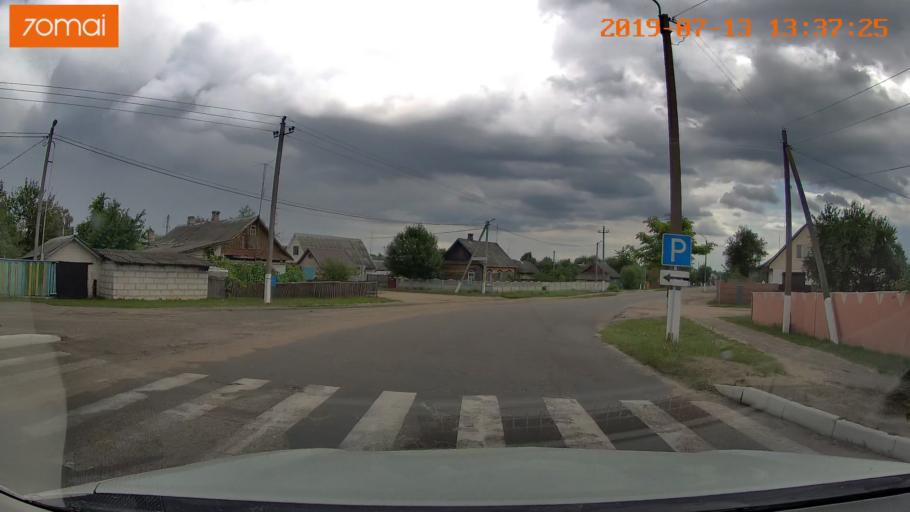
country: BY
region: Mogilev
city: Asipovichy
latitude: 53.3010
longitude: 28.6249
